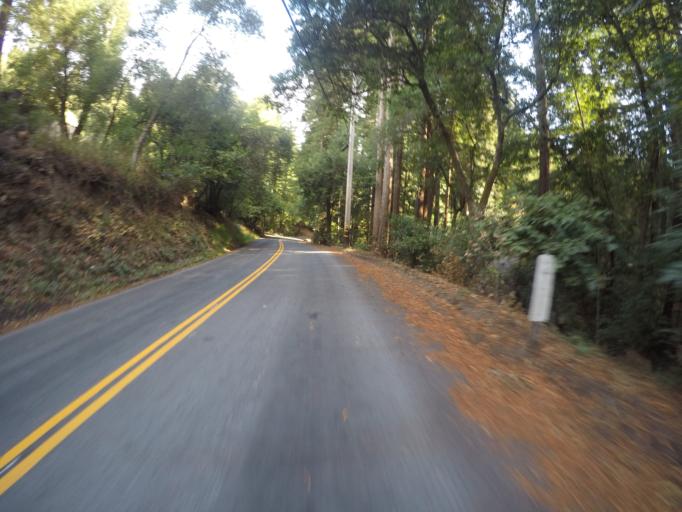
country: US
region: California
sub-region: Santa Cruz County
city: Scotts Valley
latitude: 37.0555
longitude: -121.9727
